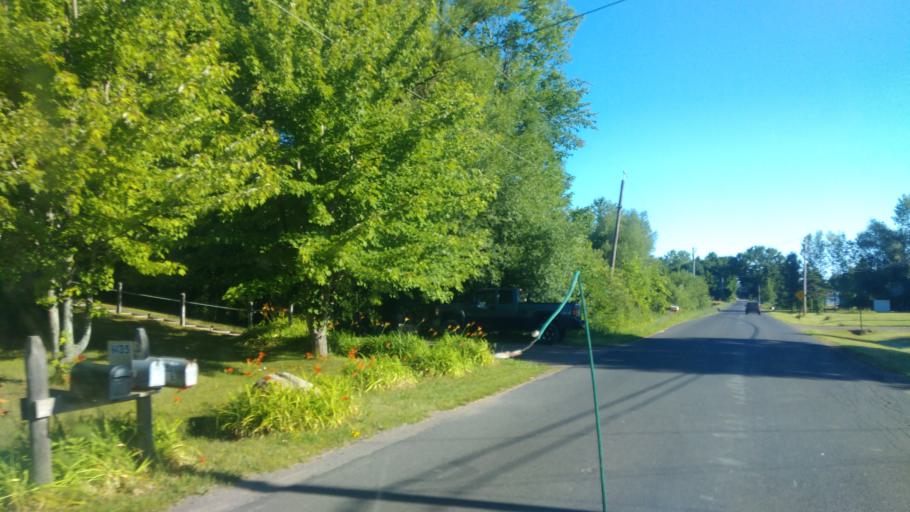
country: US
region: New York
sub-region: Wayne County
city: Sodus
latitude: 43.2329
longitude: -77.1110
